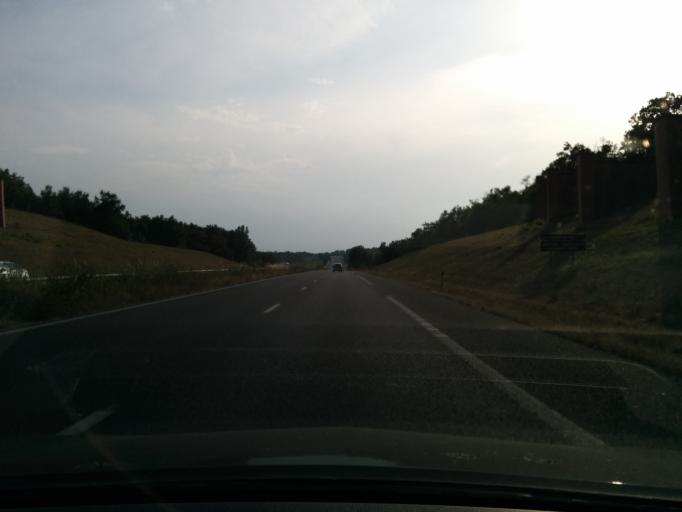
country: FR
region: Midi-Pyrenees
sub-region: Departement de la Haute-Garonne
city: Montastruc-la-Conseillere
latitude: 43.7470
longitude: 1.6137
